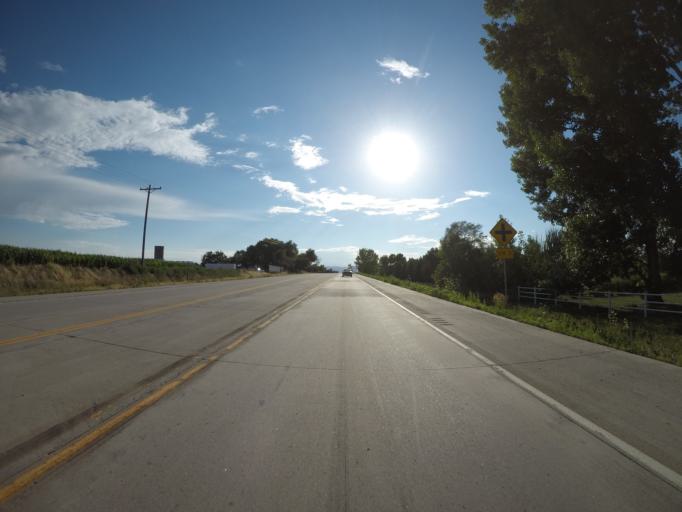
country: US
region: Colorado
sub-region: Weld County
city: Windsor
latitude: 40.5810
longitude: -104.9603
